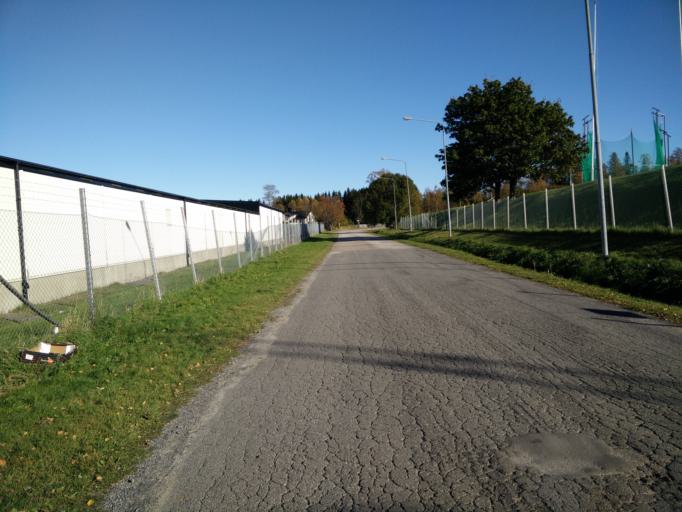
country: SE
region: Vaesternorrland
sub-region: Haernoesands Kommun
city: Haernoesand
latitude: 62.6388
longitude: 17.9658
